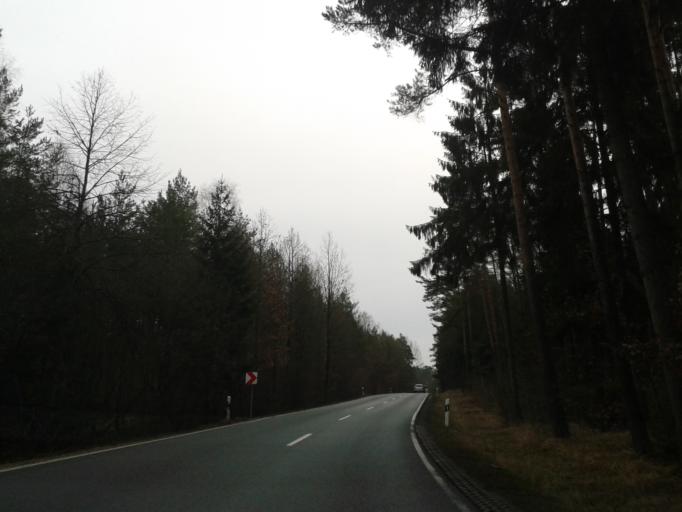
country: DE
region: Bavaria
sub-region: Upper Franconia
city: Weitramsdorf
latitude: 50.2329
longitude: 10.8916
